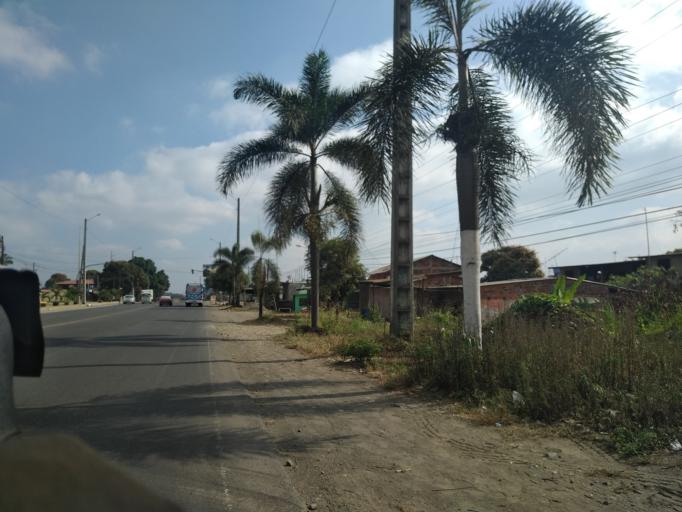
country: EC
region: Los Rios
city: Quevedo
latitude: -1.0582
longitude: -79.4882
